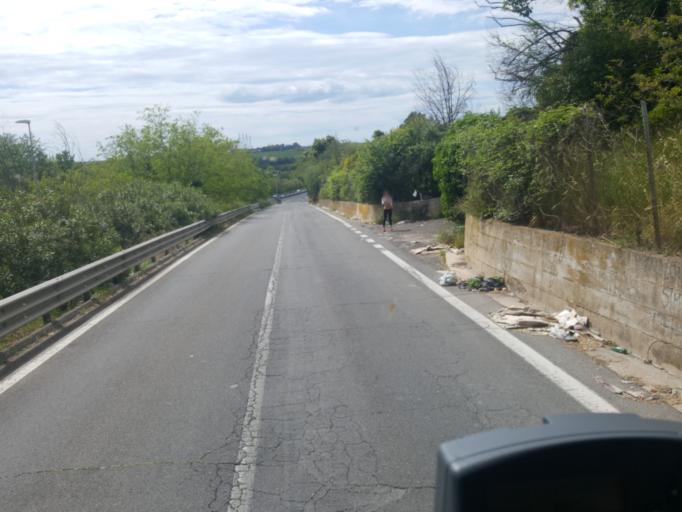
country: IT
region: Latium
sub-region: Citta metropolitana di Roma Capitale
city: La Massimina-Casal Lumbroso
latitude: 41.8825
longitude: 12.3449
